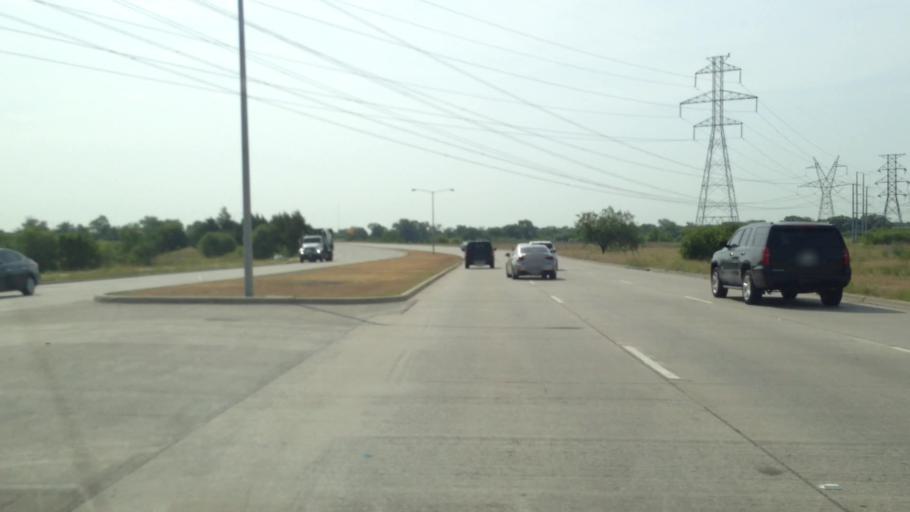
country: US
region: Texas
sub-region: Denton County
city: Lewisville
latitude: 33.0132
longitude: -96.9566
